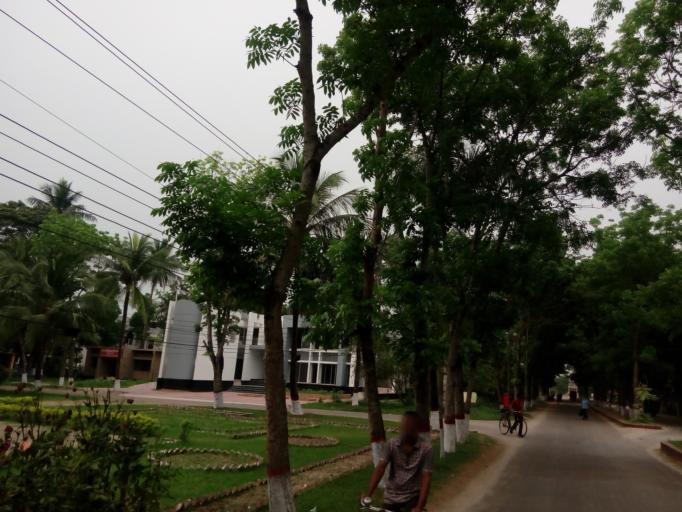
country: BD
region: Khulna
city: Khulna
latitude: 22.8005
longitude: 89.5343
